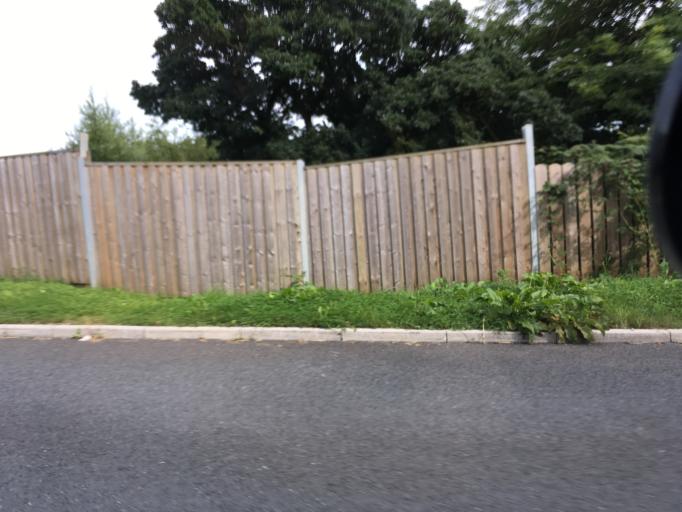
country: IE
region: Leinster
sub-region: Wicklow
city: Ashford
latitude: 53.0421
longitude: -6.0901
